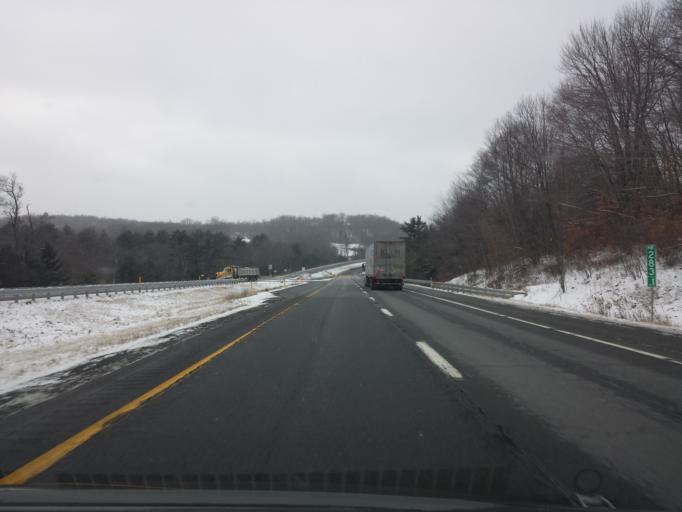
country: US
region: Pennsylvania
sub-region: Carbon County
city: Towamensing Trails
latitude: 41.0771
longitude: -75.5870
